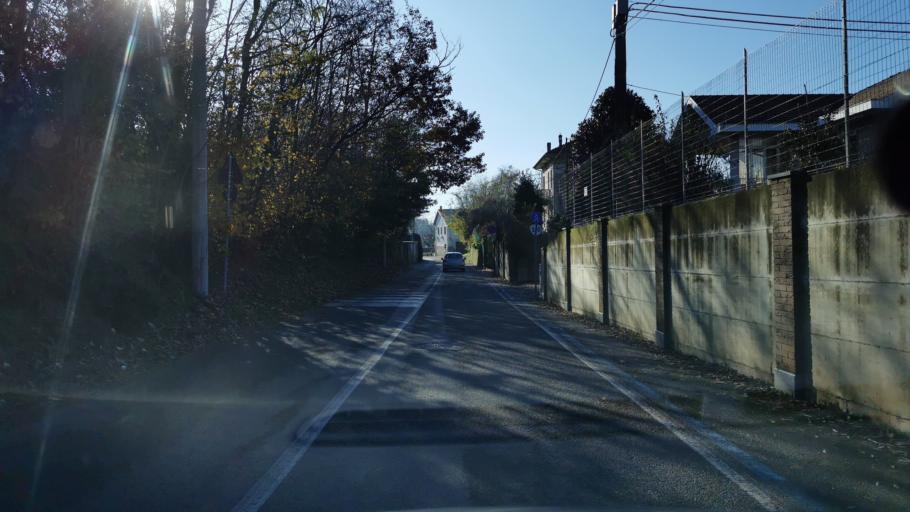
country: IT
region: Piedmont
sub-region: Provincia di Torino
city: Fiano
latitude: 45.2133
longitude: 7.5244
